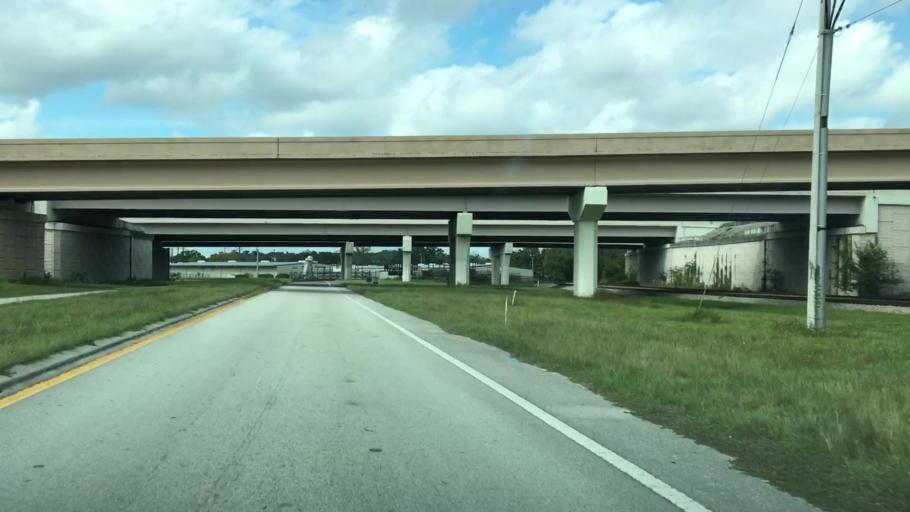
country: US
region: Florida
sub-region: Volusia County
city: DeBary
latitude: 28.8291
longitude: -81.3241
